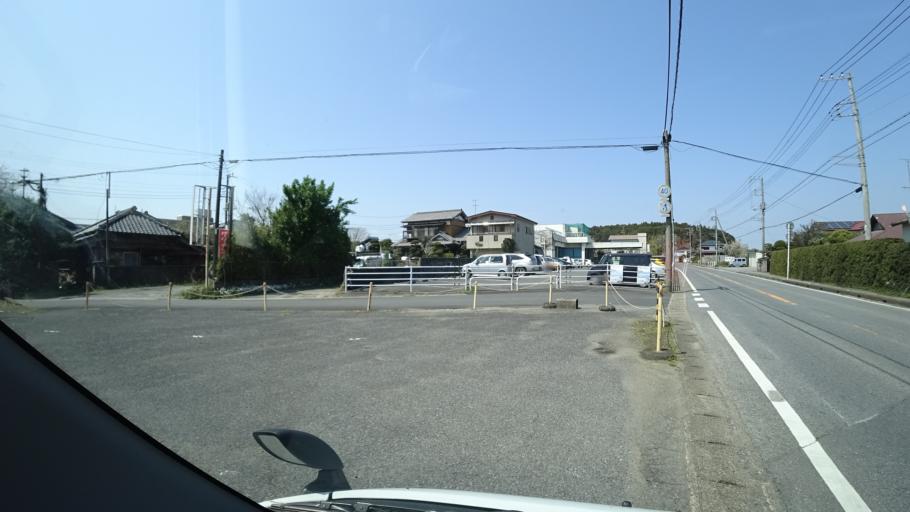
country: JP
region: Chiba
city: Yokaichiba
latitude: 35.6611
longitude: 140.4772
